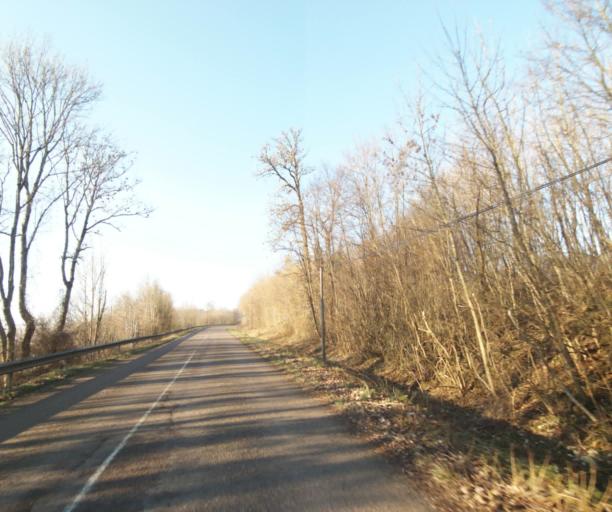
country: FR
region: Champagne-Ardenne
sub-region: Departement de la Haute-Marne
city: Chevillon
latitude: 48.5469
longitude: 5.0989
